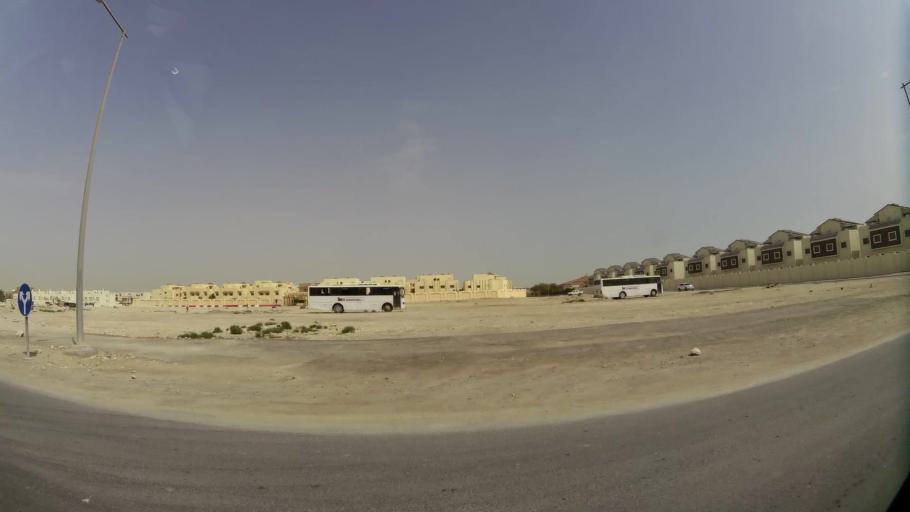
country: QA
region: Baladiyat ad Dawhah
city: Doha
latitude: 25.3010
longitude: 51.4825
